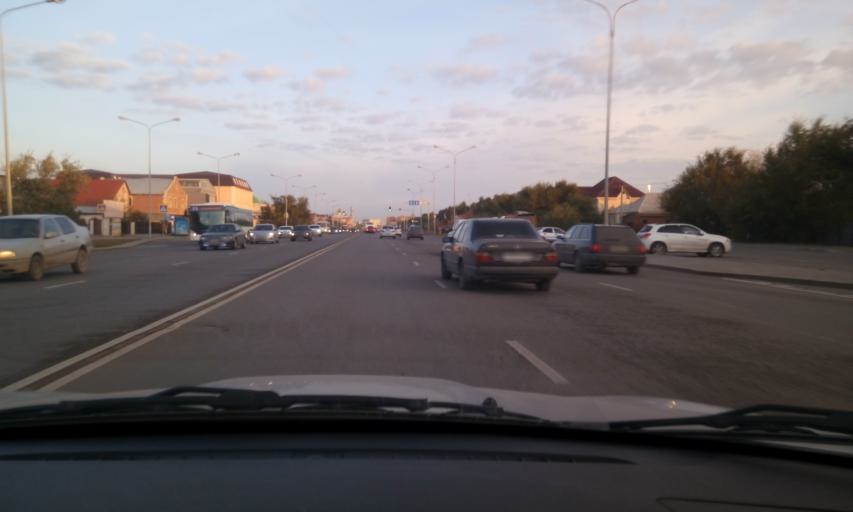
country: KZ
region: Astana Qalasy
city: Astana
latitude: 51.1356
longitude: 71.4926
